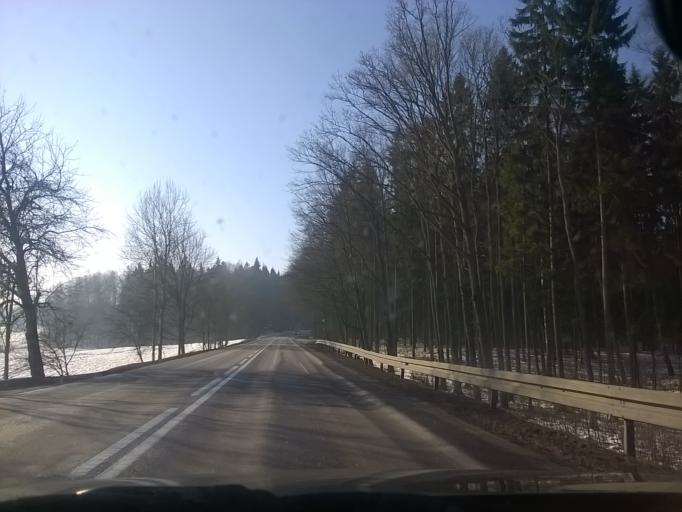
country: PL
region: Warmian-Masurian Voivodeship
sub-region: Powiat olsztynski
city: Biskupiec
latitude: 53.8405
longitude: 21.1179
